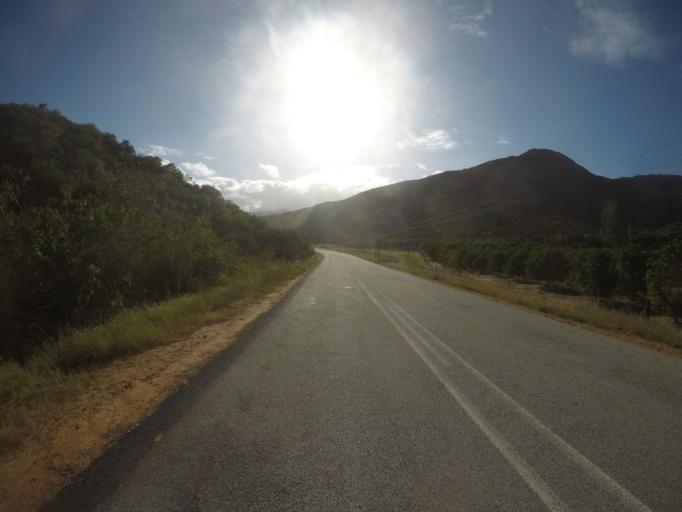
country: ZA
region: Western Cape
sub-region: West Coast District Municipality
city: Clanwilliam
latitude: -32.4379
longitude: 18.9440
